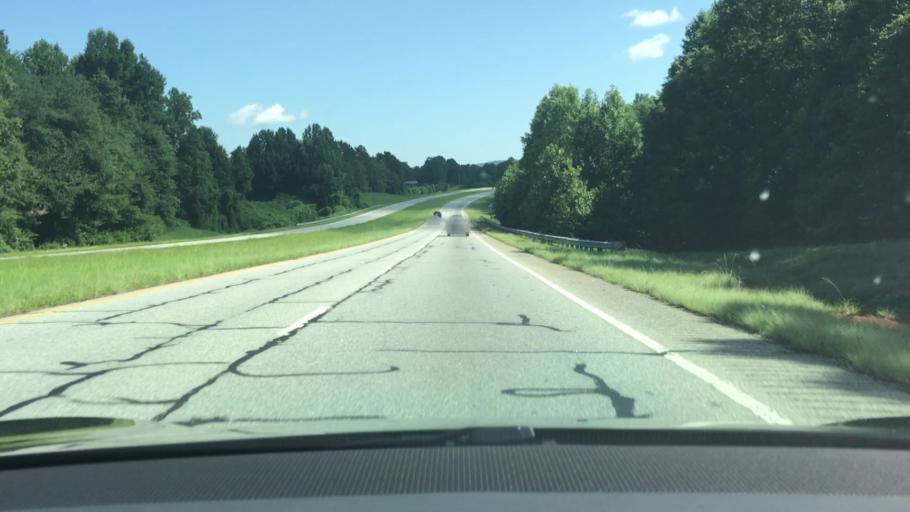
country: US
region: Georgia
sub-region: Habersham County
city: Clarkesville
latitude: 34.6675
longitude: -83.4320
